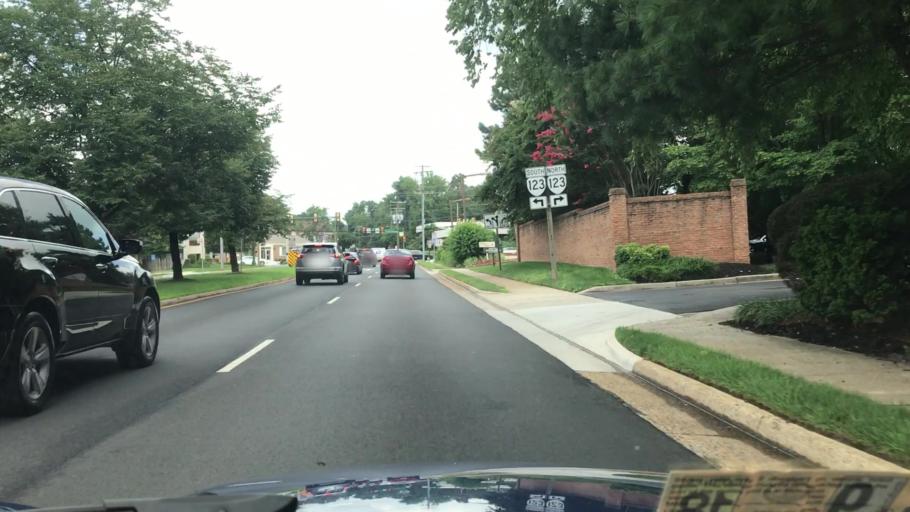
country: US
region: Virginia
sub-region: Fairfax County
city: Vienna
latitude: 38.8936
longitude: -77.2730
